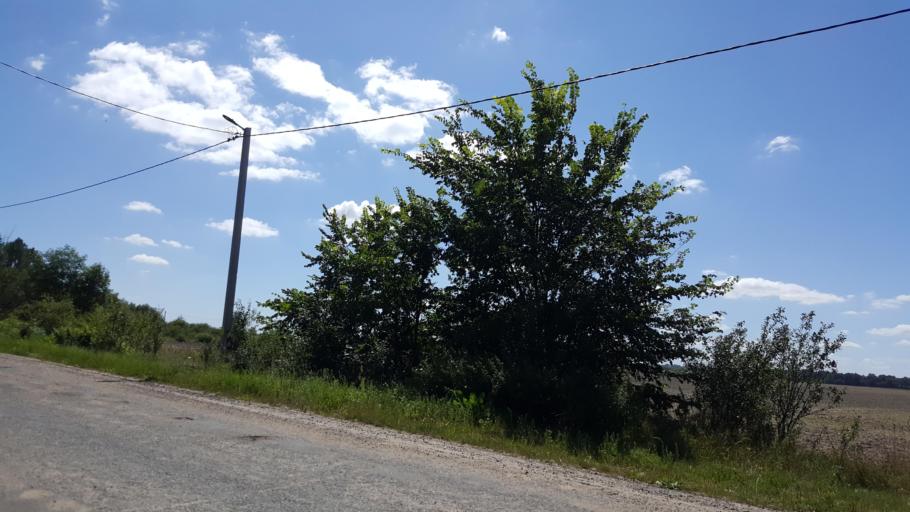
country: BY
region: Brest
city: Horad Kobryn
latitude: 52.3332
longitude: 24.3736
